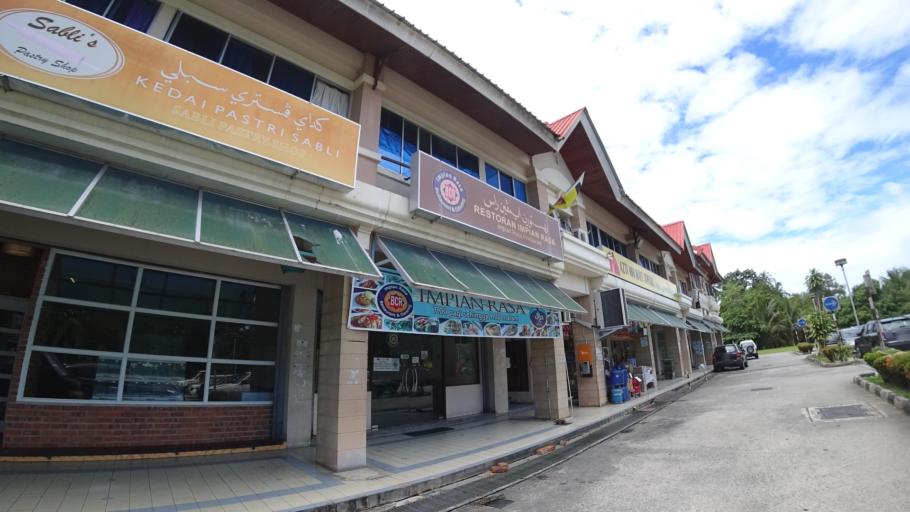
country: BN
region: Tutong
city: Tutong
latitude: 4.7680
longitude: 114.8223
